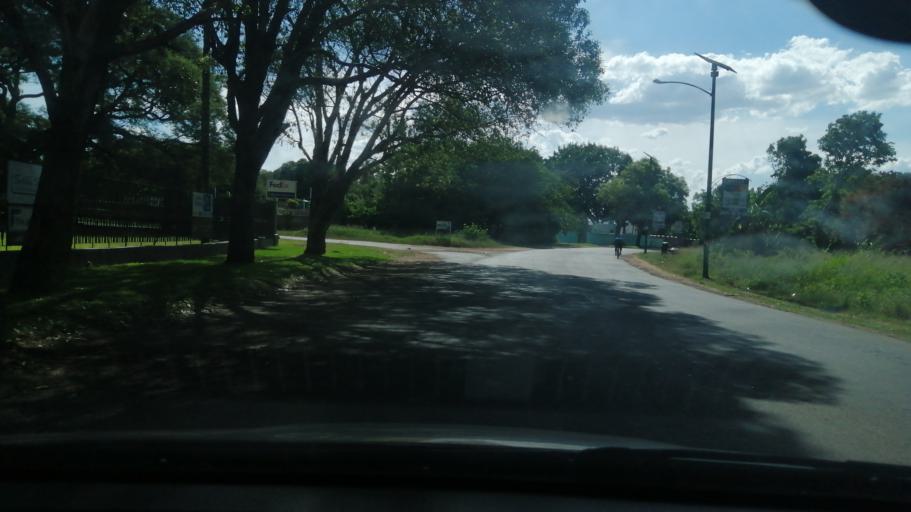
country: ZW
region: Harare
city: Harare
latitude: -17.7905
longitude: 31.0593
